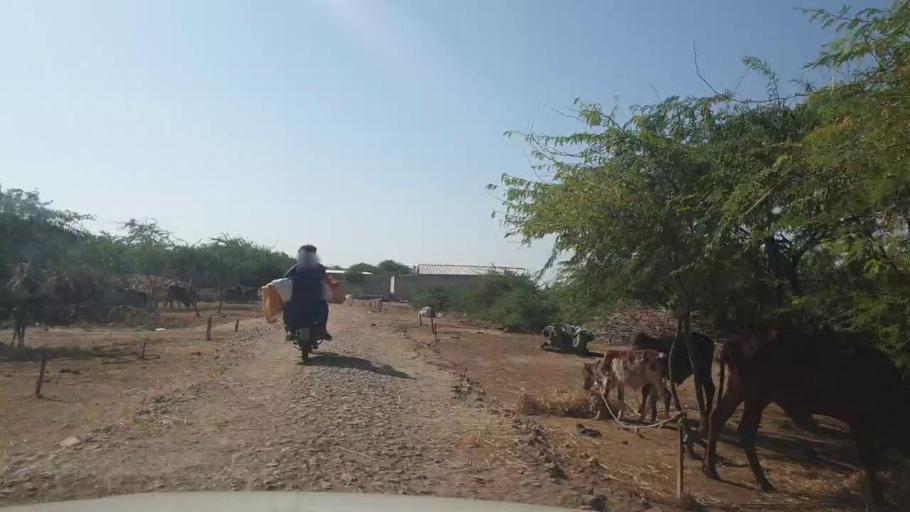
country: PK
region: Sindh
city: Chuhar Jamali
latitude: 24.4369
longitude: 67.8417
